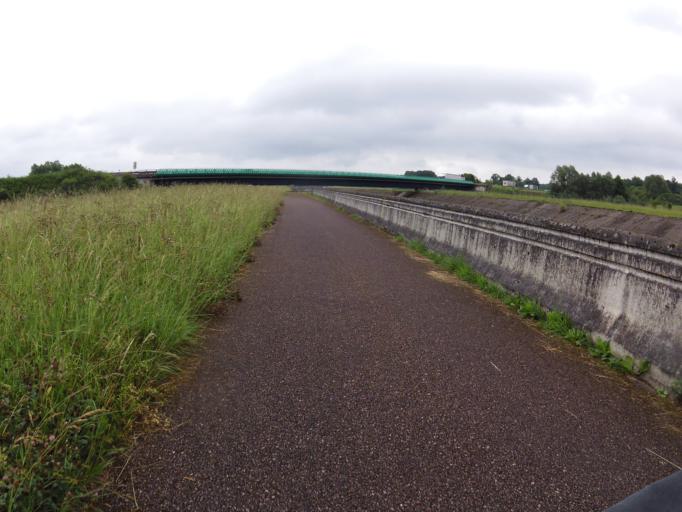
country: FR
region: Champagne-Ardenne
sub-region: Departement de la Haute-Marne
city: Saint-Dizier
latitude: 48.6222
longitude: 4.9388
